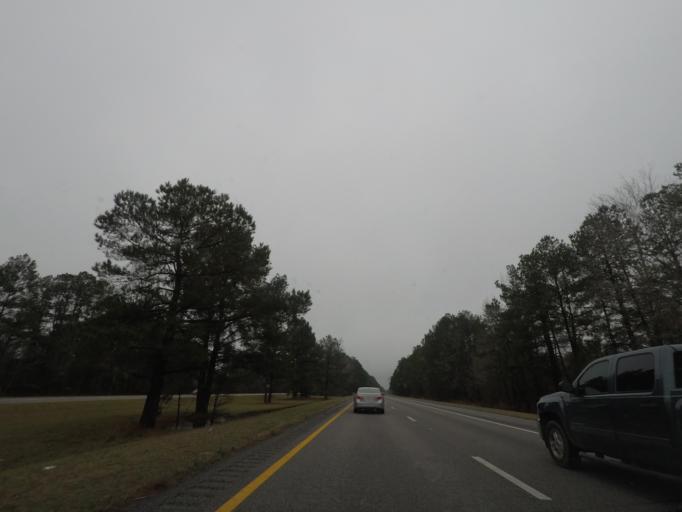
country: US
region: South Carolina
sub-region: Sumter County
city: East Sumter
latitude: 33.9318
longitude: -80.0688
